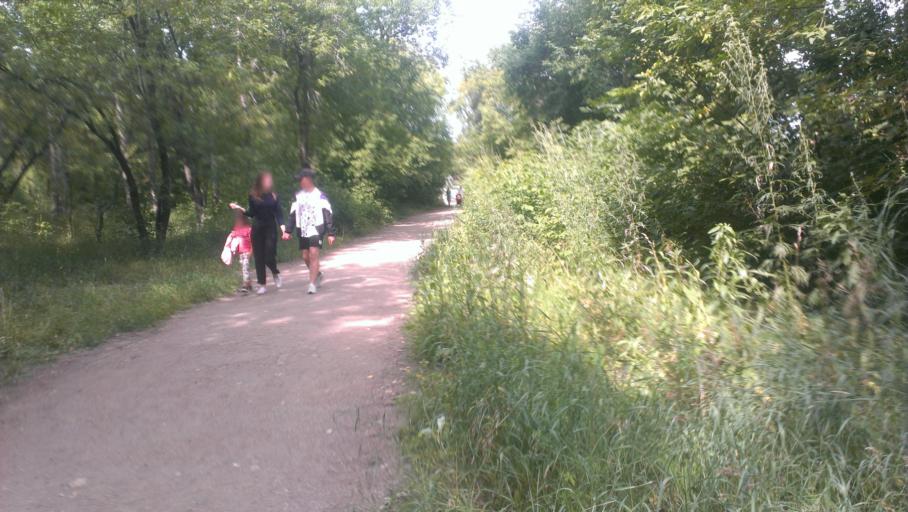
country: RU
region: Altai Krai
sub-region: Gorod Barnaulskiy
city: Barnaul
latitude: 53.3594
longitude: 83.6890
